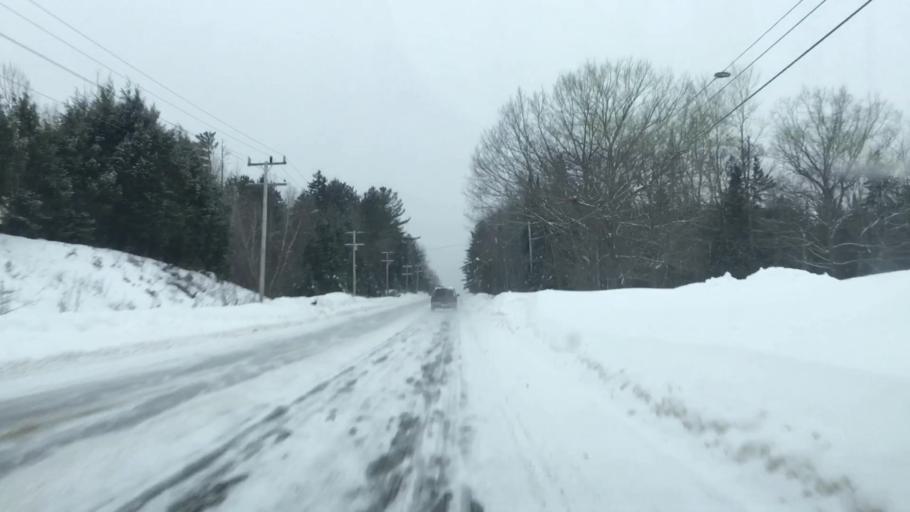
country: US
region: Maine
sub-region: Penobscot County
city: Medway
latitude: 45.5988
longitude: -68.4712
